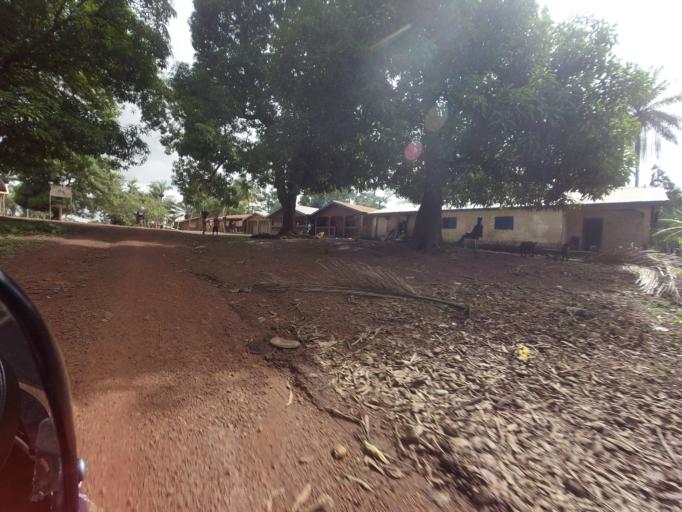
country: SL
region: Northern Province
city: Kambia
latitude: 9.0858
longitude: -13.0172
